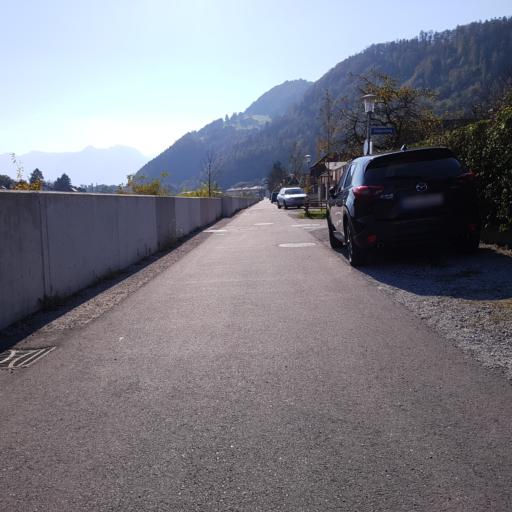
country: AT
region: Salzburg
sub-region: Politischer Bezirk Hallein
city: Hallein
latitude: 47.6802
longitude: 13.0974
